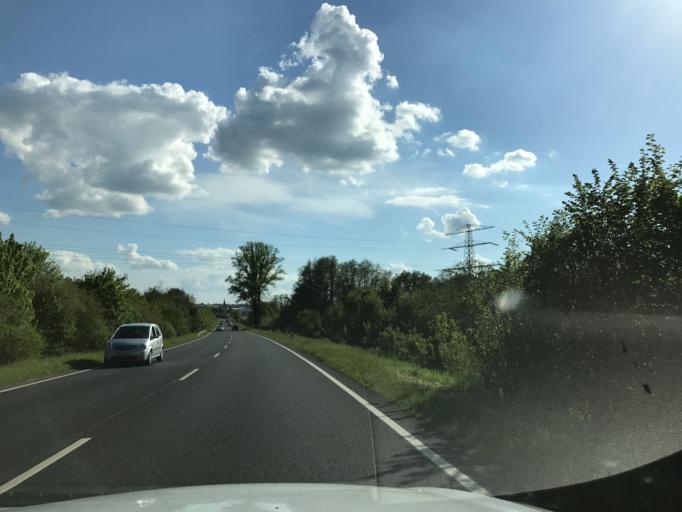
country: DE
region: Bavaria
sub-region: Upper Franconia
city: Igensdorf
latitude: 49.5860
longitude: 11.2104
